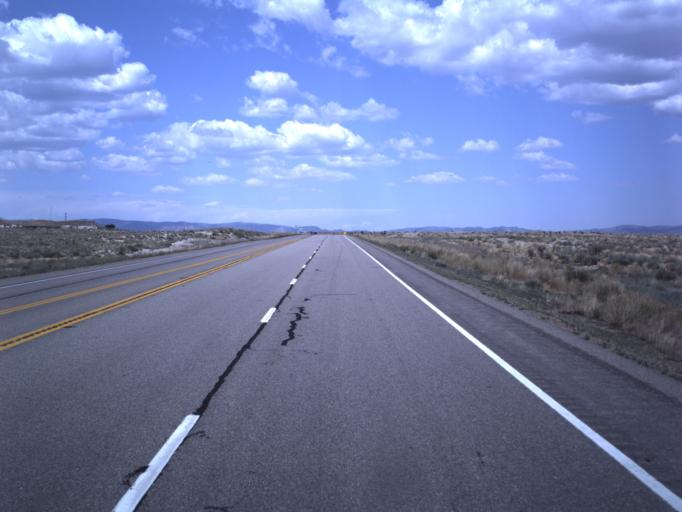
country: US
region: Utah
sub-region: Carbon County
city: Price
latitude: 39.5276
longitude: -110.8211
